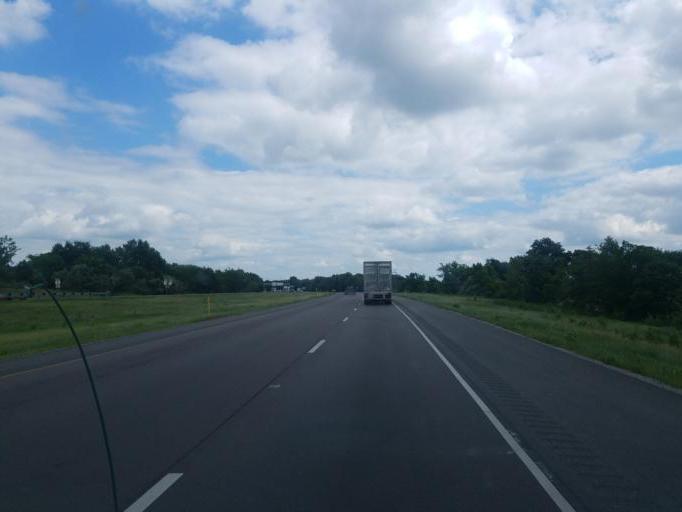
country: US
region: Illinois
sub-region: Jefferson County
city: Mount Vernon
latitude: 38.2662
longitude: -88.9322
